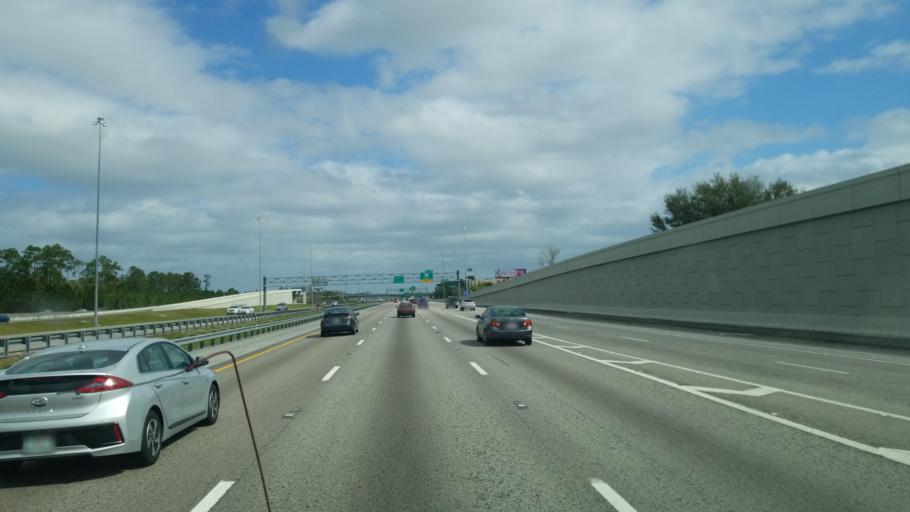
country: US
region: Florida
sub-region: Osceola County
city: Celebration
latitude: 28.3384
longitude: -81.5391
